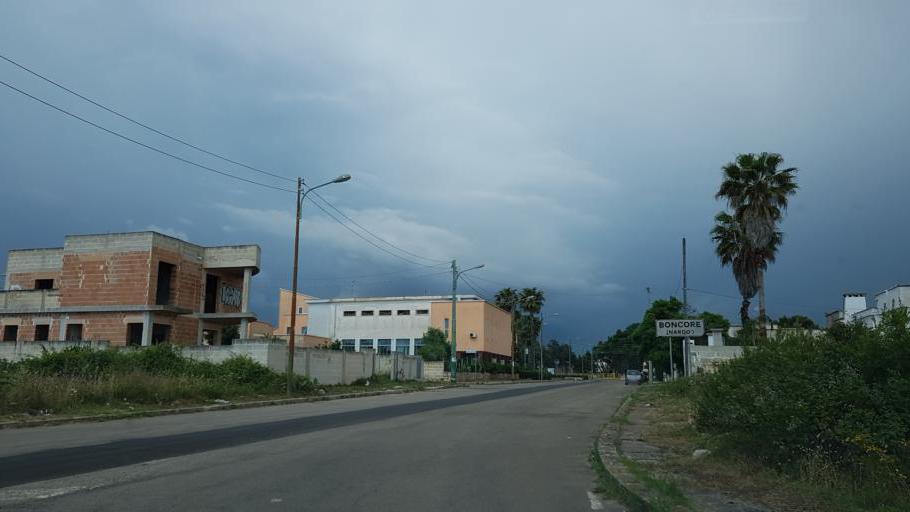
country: IT
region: Apulia
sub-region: Provincia di Lecce
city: Porto Cesareo
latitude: 40.2946
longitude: 17.8579
